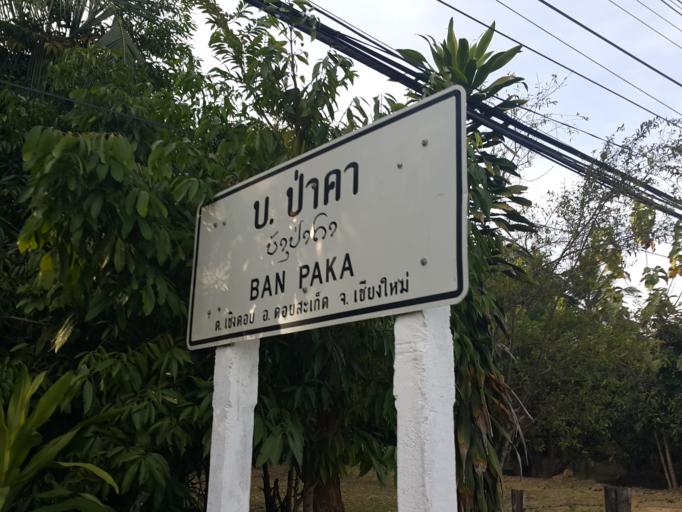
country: TH
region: Chiang Mai
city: San Sai
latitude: 18.8536
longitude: 99.1314
